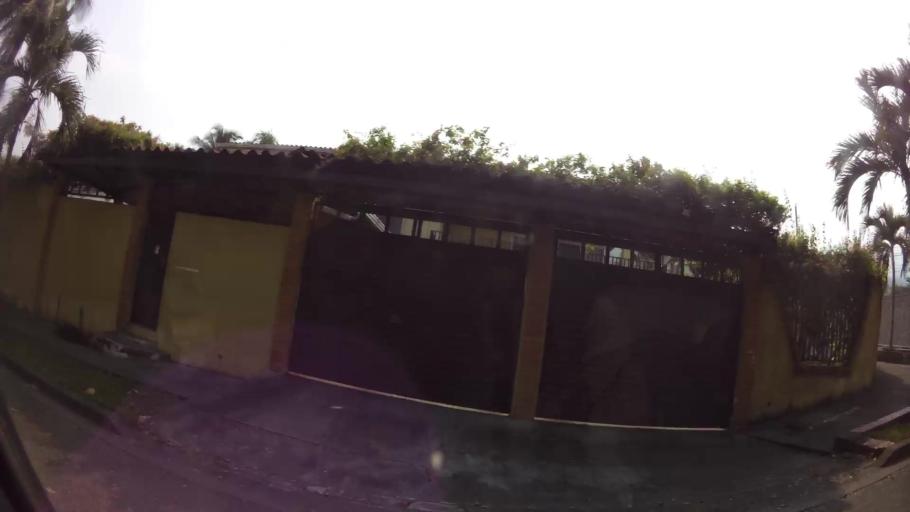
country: HN
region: Cortes
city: Armenta
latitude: 15.4945
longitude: -88.0473
